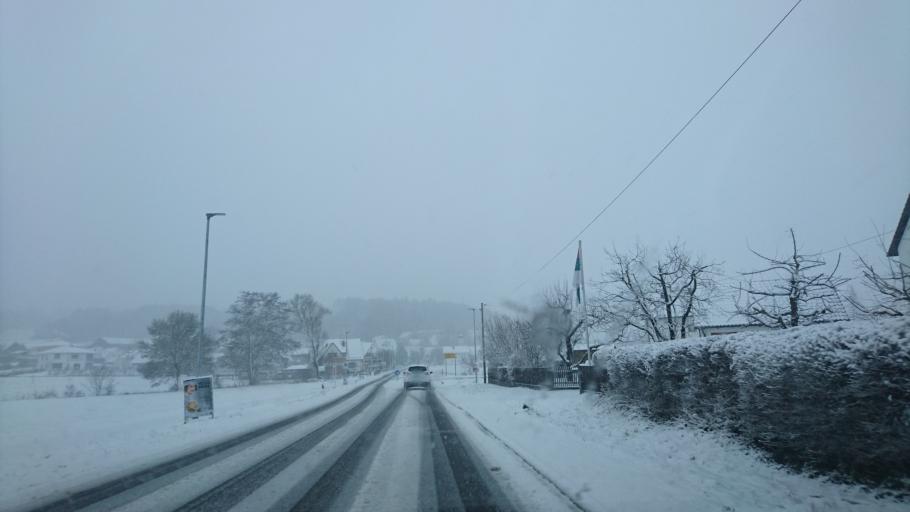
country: DE
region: Bavaria
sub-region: Swabia
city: Emersacker
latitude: 48.5140
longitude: 10.6833
